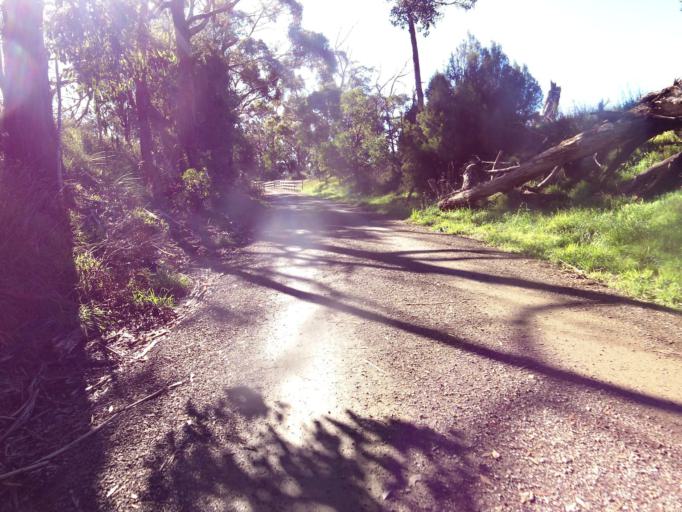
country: AU
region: Victoria
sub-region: Yarra Ranges
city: Lilydale
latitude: -37.7314
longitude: 145.3711
